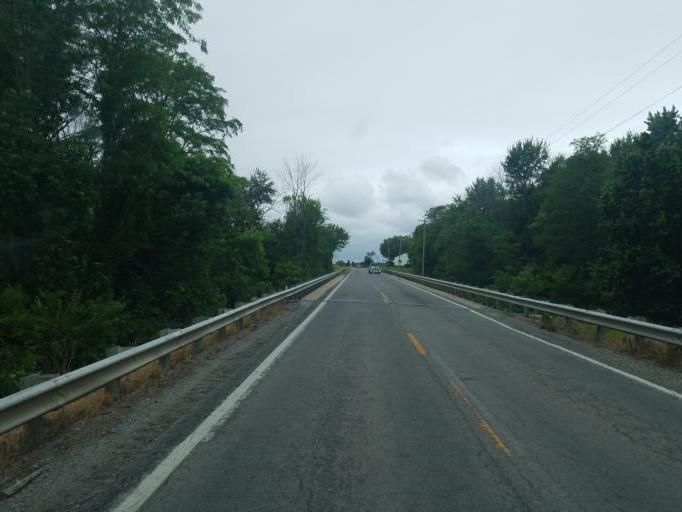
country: US
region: Ohio
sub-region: Marion County
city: Marion
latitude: 40.5439
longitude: -83.0183
